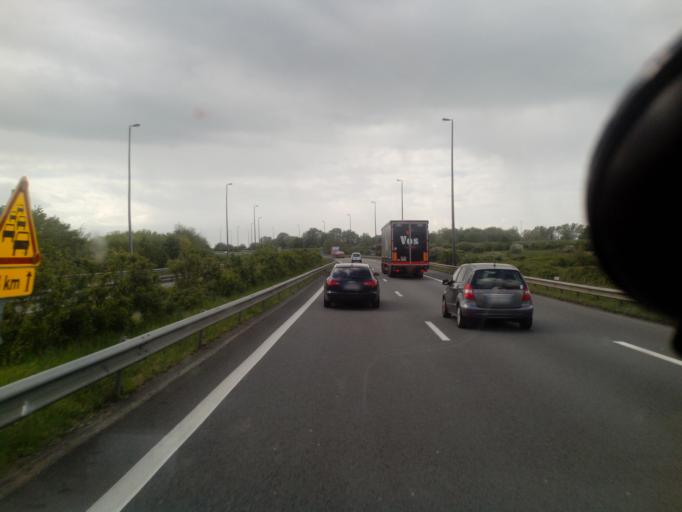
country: FR
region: Nord-Pas-de-Calais
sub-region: Departement du Pas-de-Calais
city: Coulogne
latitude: 50.9350
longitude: 1.8806
